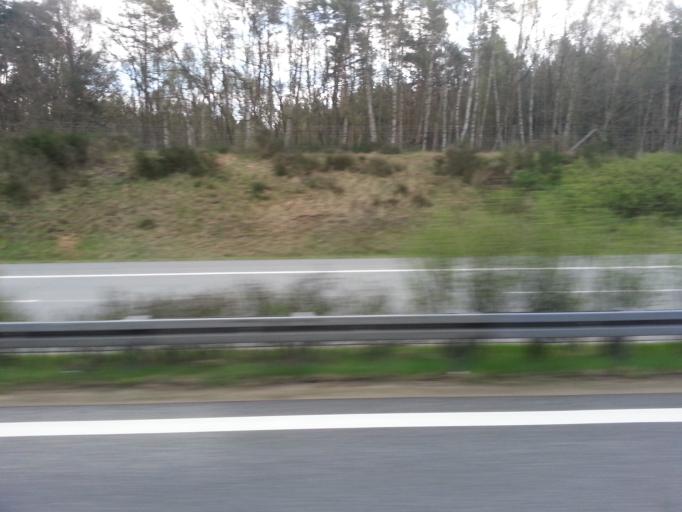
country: DE
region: Mecklenburg-Vorpommern
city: Malchow
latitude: 53.5029
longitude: 12.3781
